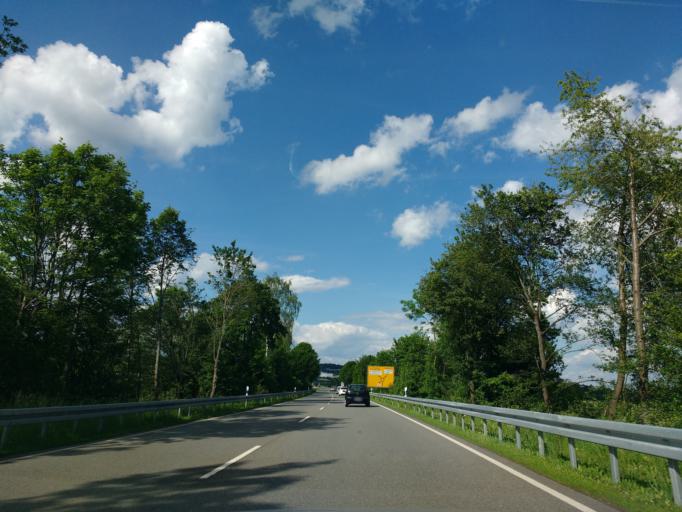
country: DE
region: Hesse
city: Allendorf
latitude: 51.0172
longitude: 8.6657
